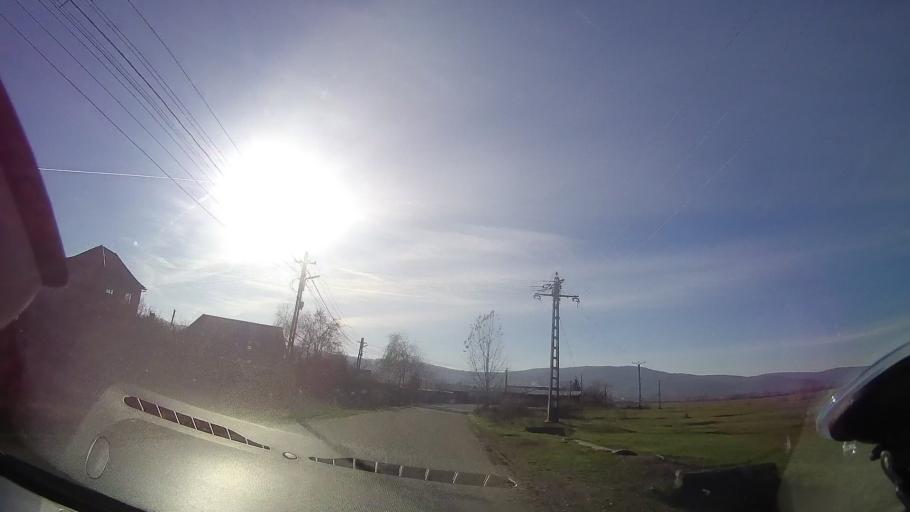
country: RO
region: Bihor
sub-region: Comuna Magesti
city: Magesti
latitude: 47.0188
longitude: 22.4678
